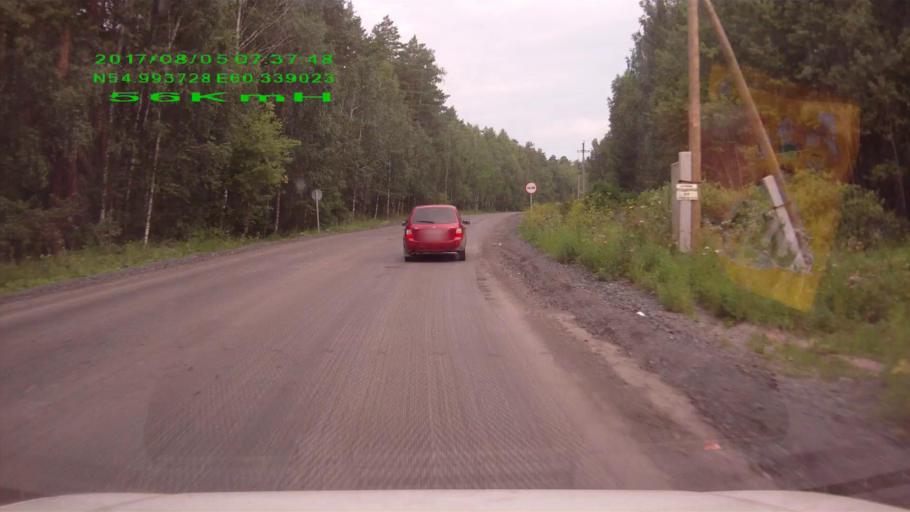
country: RU
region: Chelyabinsk
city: Chebarkul'
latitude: 54.9940
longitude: 60.3387
